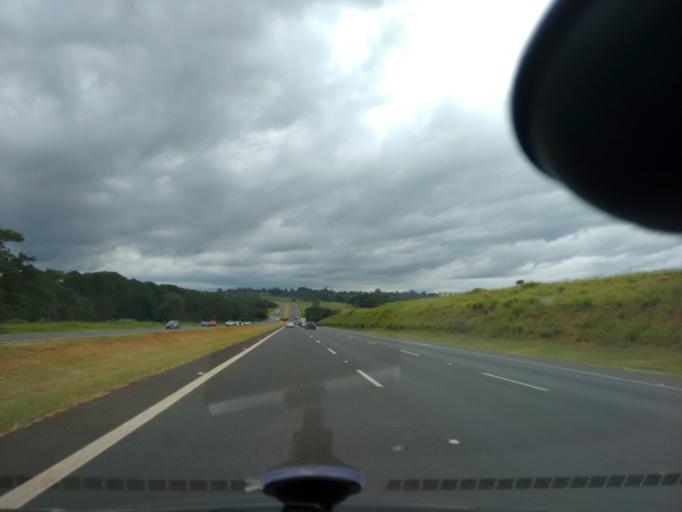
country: BR
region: Sao Paulo
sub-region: Hortolandia
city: Hortolandia
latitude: -22.9183
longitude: -47.1518
